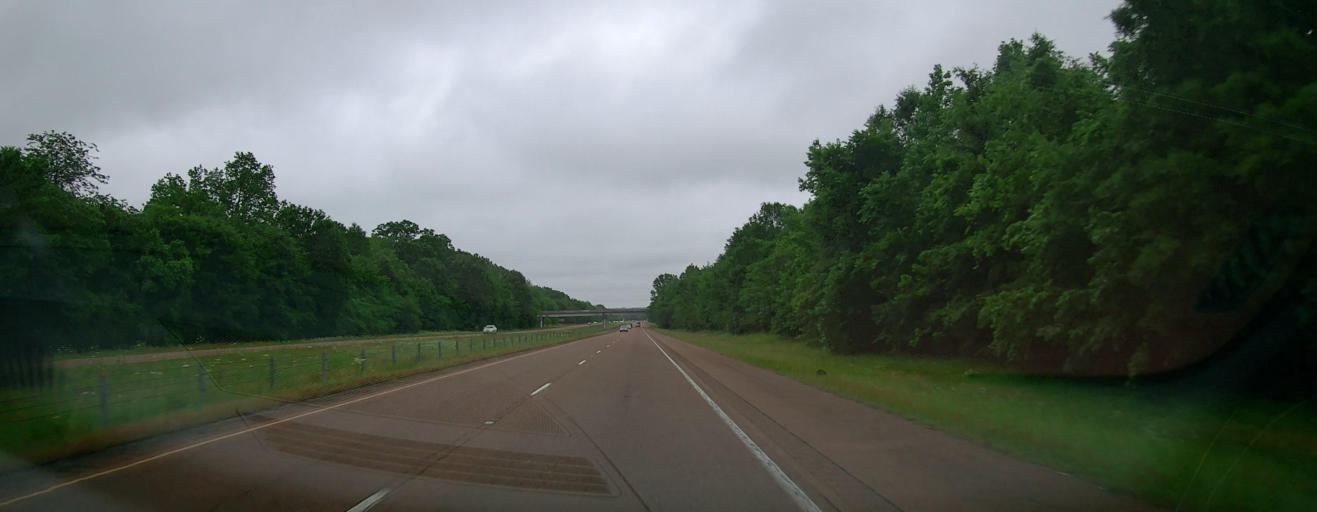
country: US
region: Mississippi
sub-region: De Soto County
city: Olive Branch
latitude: 34.9163
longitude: -89.7727
